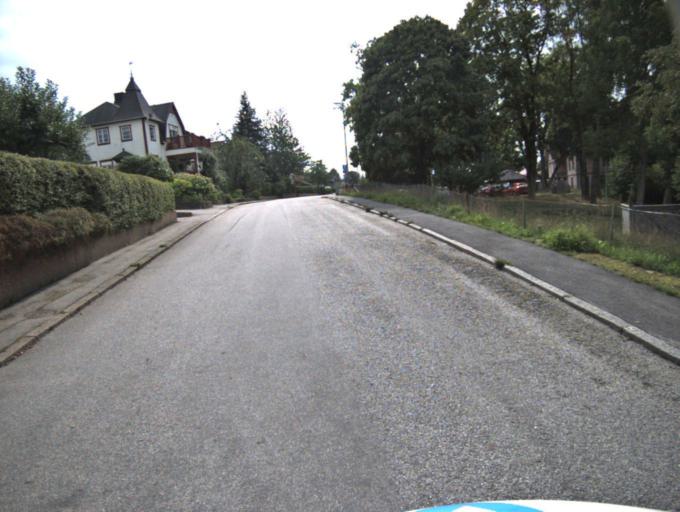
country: SE
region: Vaestra Goetaland
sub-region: Ulricehamns Kommun
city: Ulricehamn
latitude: 57.7955
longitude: 13.4187
